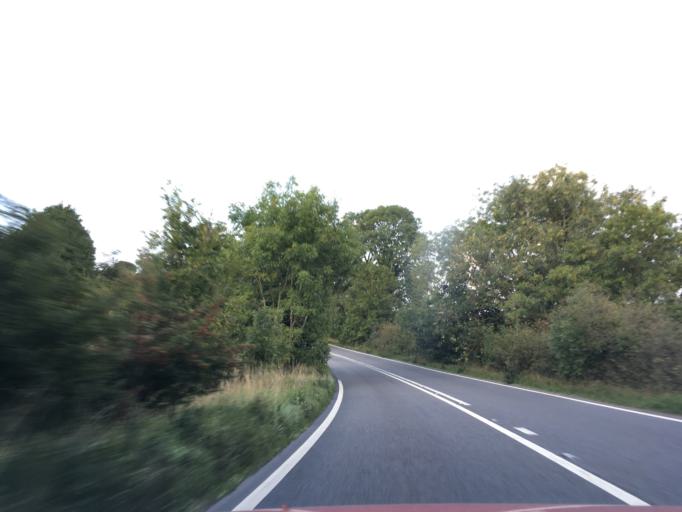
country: GB
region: England
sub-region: Gloucestershire
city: Northleach
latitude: 51.8552
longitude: -1.8044
